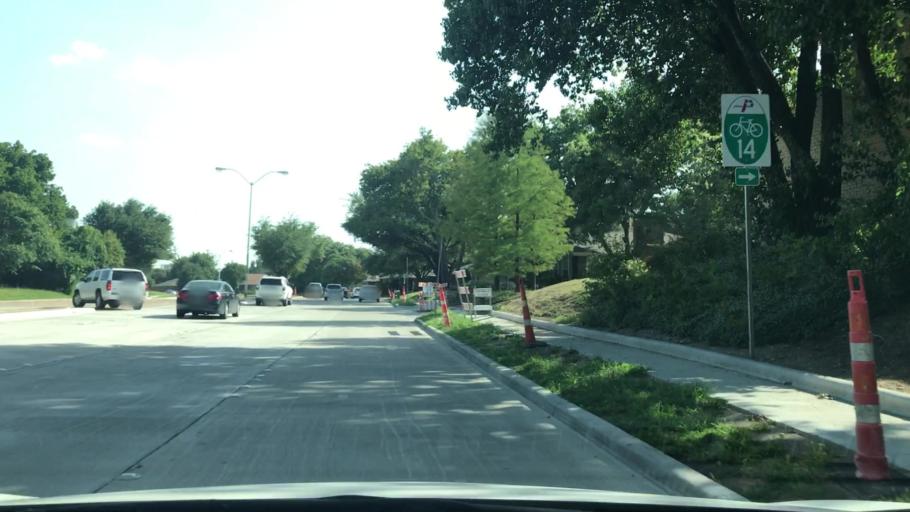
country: US
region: Texas
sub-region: Collin County
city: Plano
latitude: 33.0129
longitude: -96.7493
